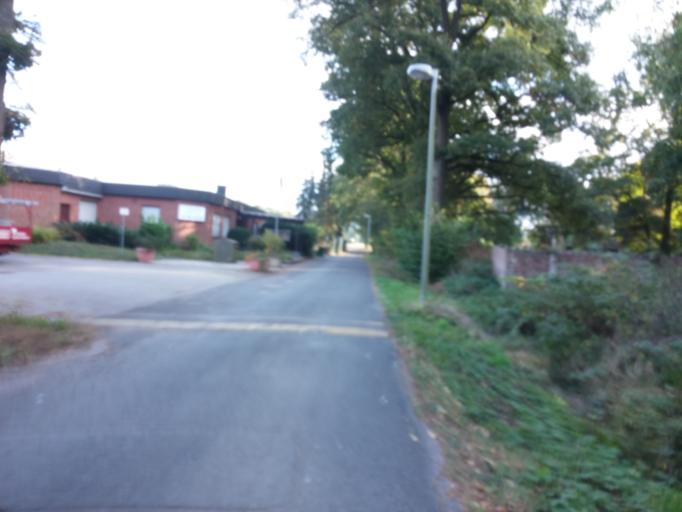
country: DE
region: North Rhine-Westphalia
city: Dorsten
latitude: 51.6464
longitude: 6.9672
